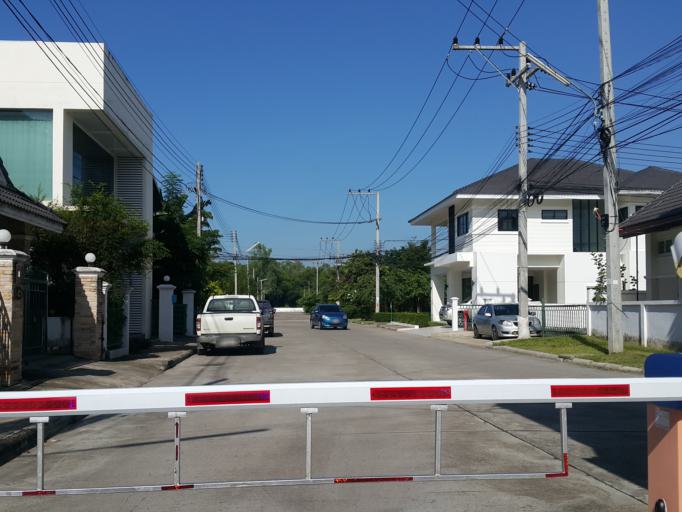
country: TH
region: Chiang Mai
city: Saraphi
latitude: 18.7746
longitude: 99.0522
